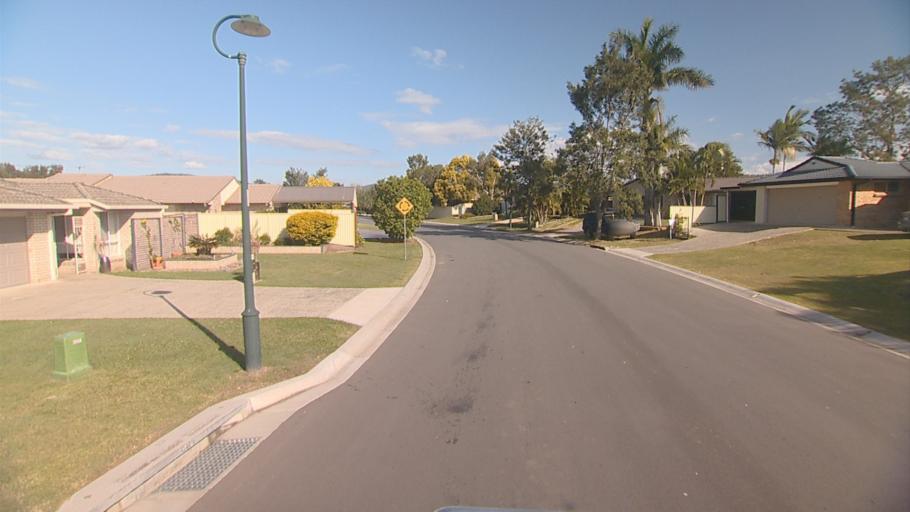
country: AU
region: Queensland
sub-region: Logan
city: Windaroo
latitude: -27.7496
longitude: 153.1944
